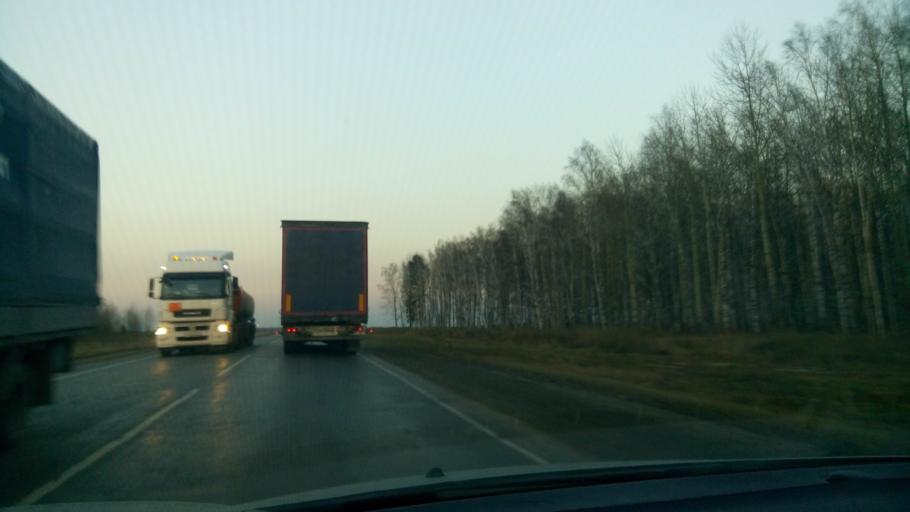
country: RU
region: Sverdlovsk
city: Pyshma
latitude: 56.9115
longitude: 63.1175
